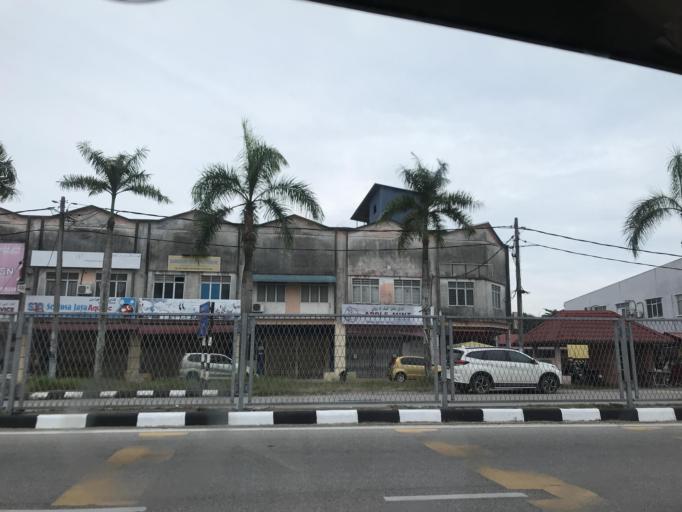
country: MY
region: Kelantan
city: Kota Bharu
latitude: 6.1148
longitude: 102.2145
